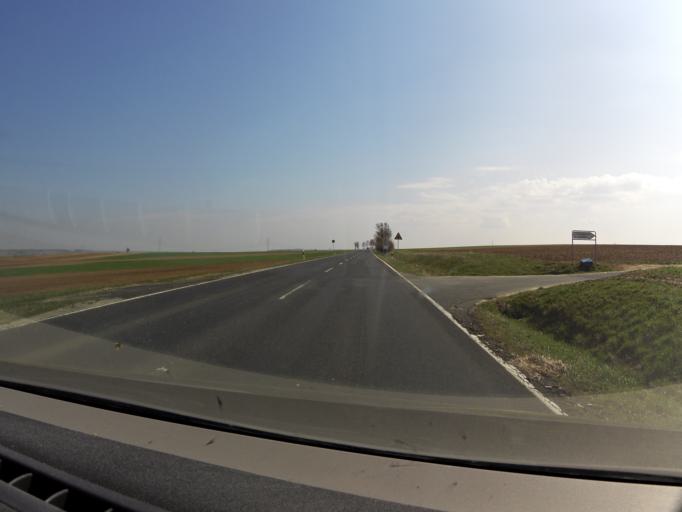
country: DE
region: Bavaria
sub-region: Regierungsbezirk Unterfranken
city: Oberpleichfeld
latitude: 49.8515
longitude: 10.0707
